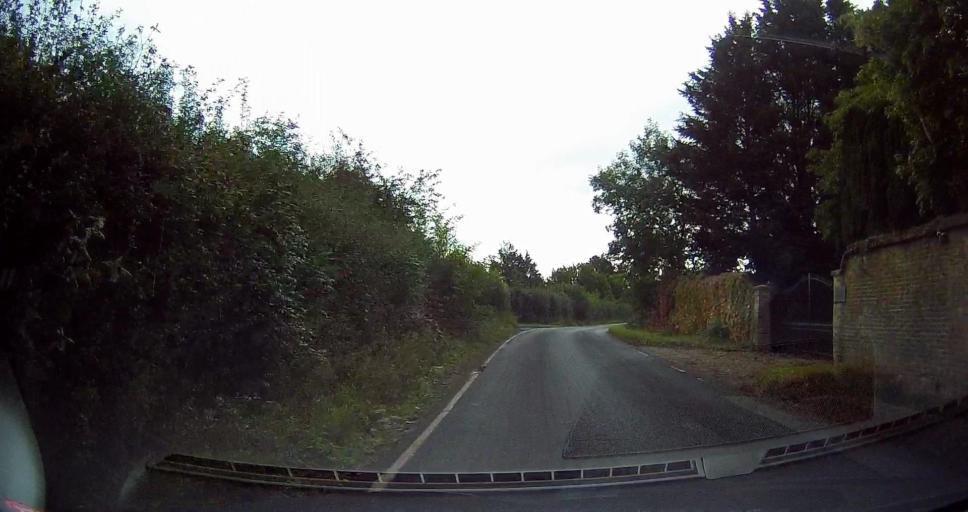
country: GB
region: England
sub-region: Kent
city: Hadlow
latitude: 51.2175
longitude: 0.3109
